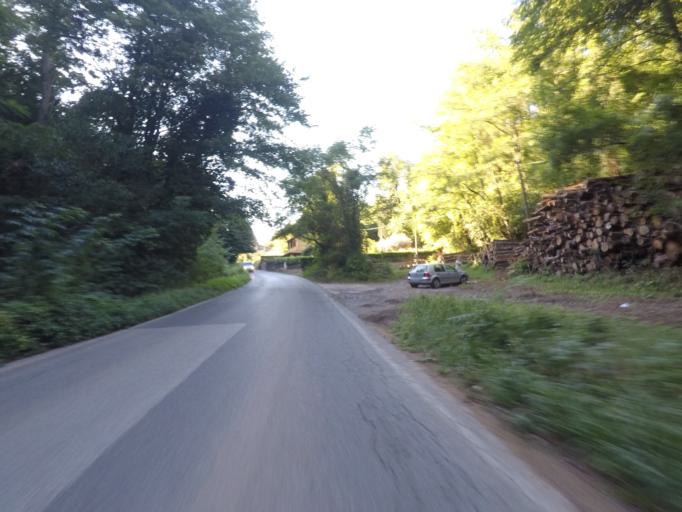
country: IT
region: Tuscany
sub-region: Provincia di Lucca
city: Stiava
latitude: 43.9058
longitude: 10.3509
